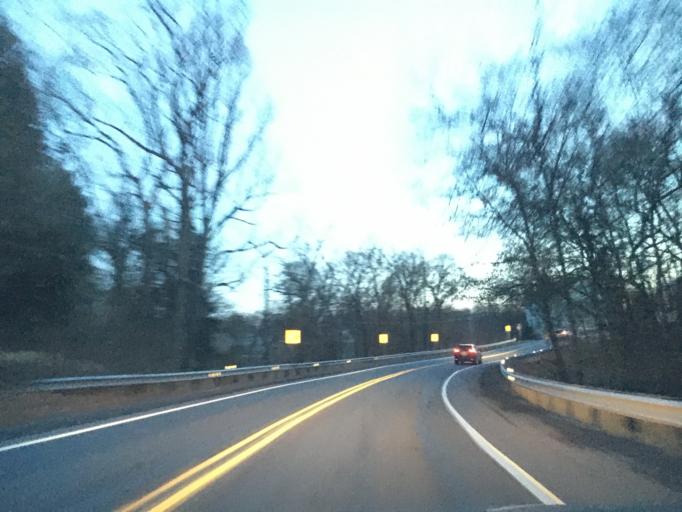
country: US
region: Pennsylvania
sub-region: Northampton County
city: Cherryville
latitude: 40.7365
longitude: -75.5434
